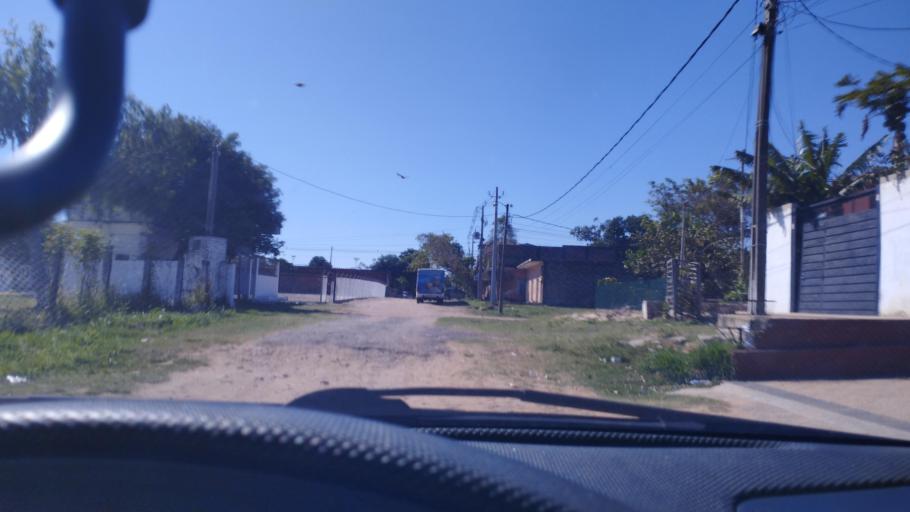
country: PY
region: Presidente Hayes
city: Nanawa
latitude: -25.2979
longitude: -57.6673
